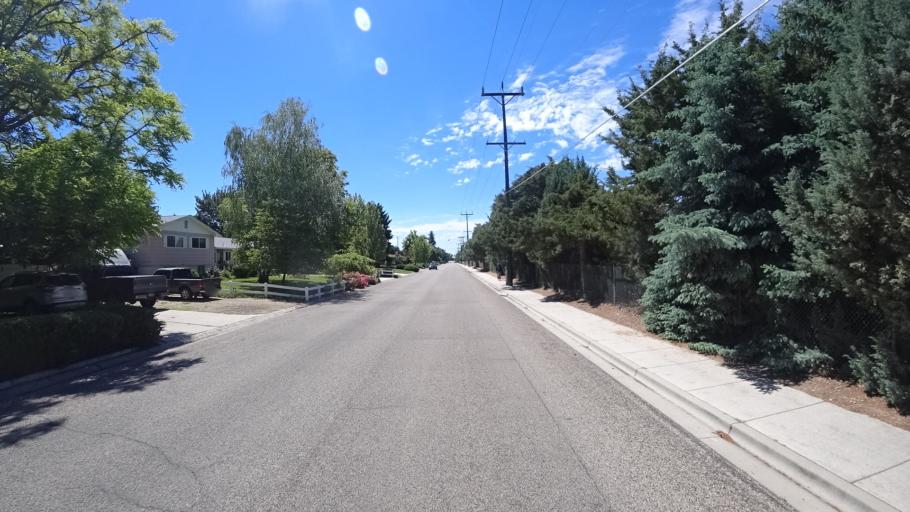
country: US
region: Idaho
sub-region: Ada County
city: Garden City
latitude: 43.5790
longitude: -116.2336
